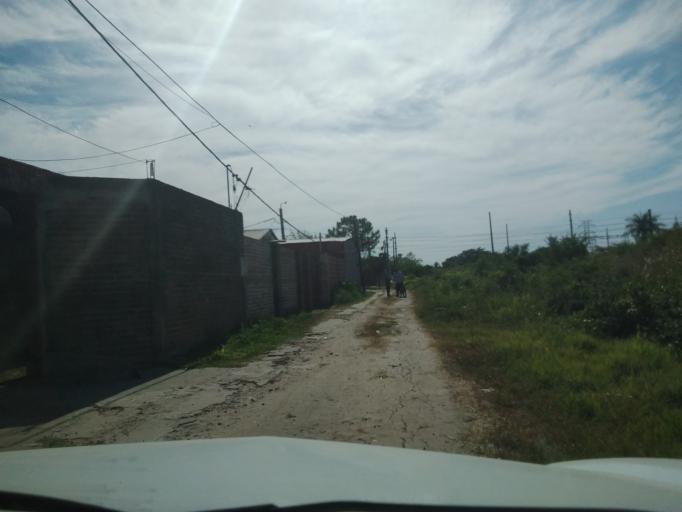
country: AR
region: Corrientes
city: Corrientes
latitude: -27.5132
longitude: -58.8000
